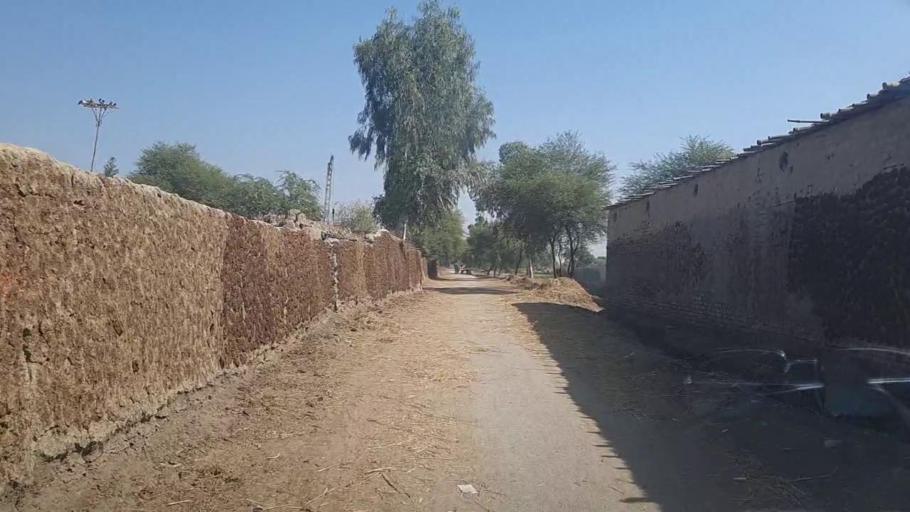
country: PK
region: Sindh
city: Thul
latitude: 28.2473
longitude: 68.8092
